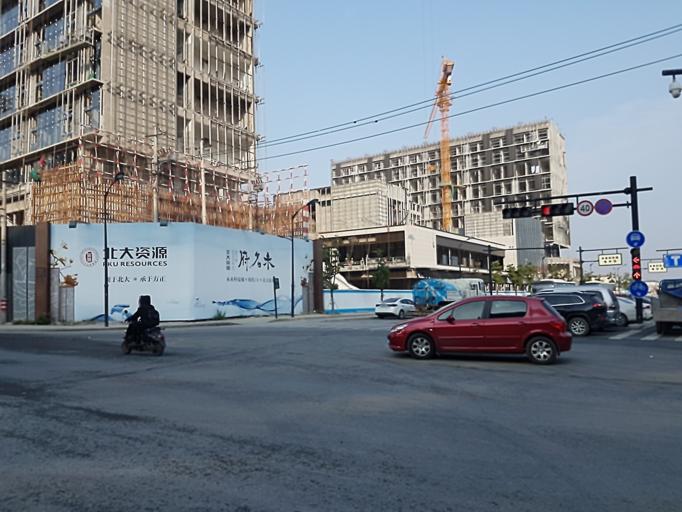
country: CN
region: Zhejiang Sheng
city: Jiangcun
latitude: 30.2961
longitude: 120.0391
